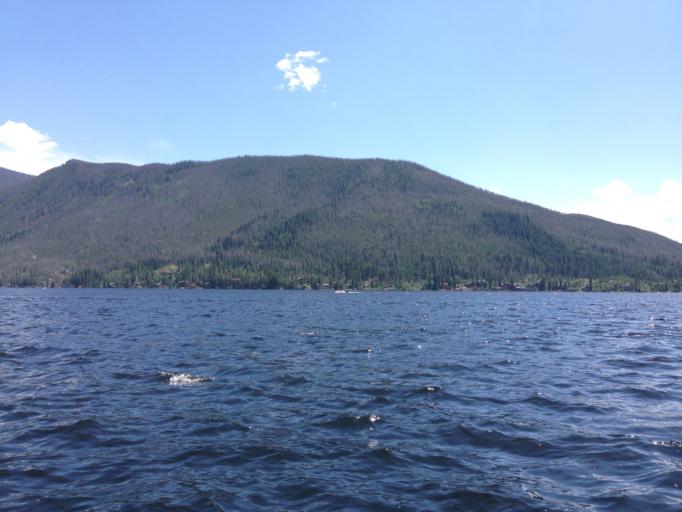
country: US
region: Colorado
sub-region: Grand County
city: Granby
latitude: 40.2505
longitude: -105.8199
